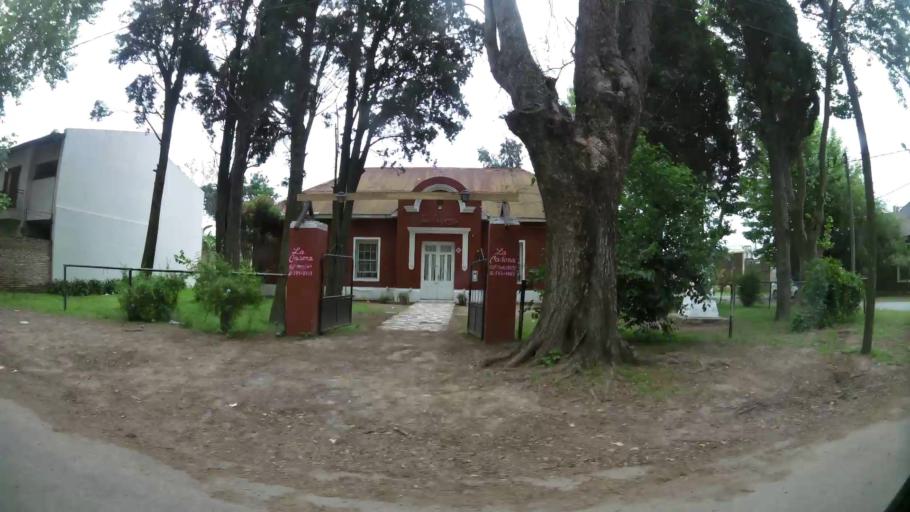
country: AR
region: Buenos Aires
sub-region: Partido de Zarate
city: Zarate
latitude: -34.1121
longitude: -59.0104
